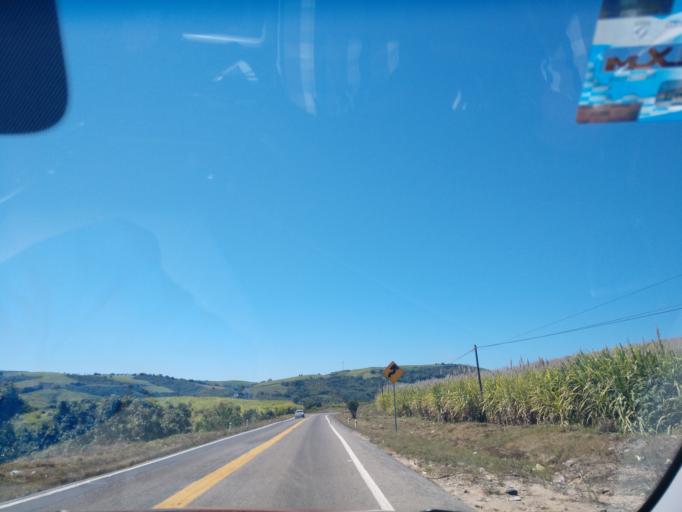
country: MX
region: Nayarit
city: Xalisco
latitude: 21.3709
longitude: -104.9063
